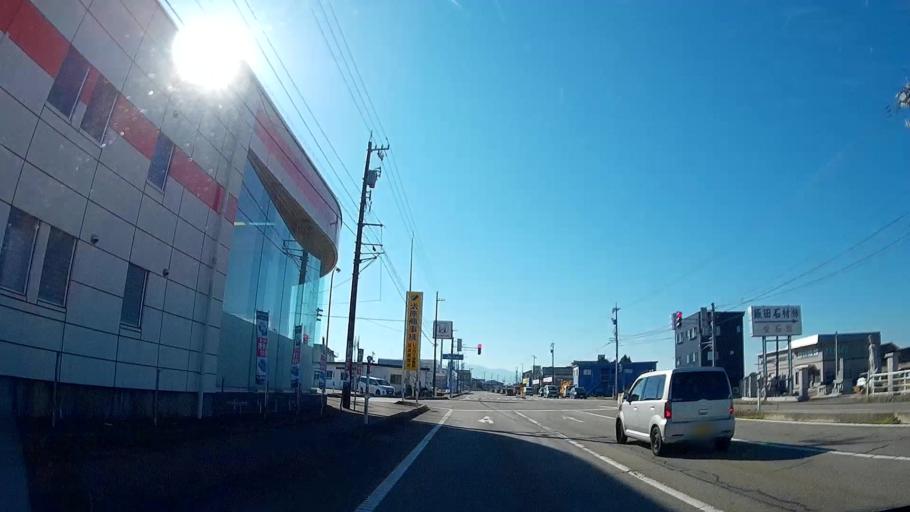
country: JP
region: Toyama
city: Takaoka
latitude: 36.6643
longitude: 136.9723
